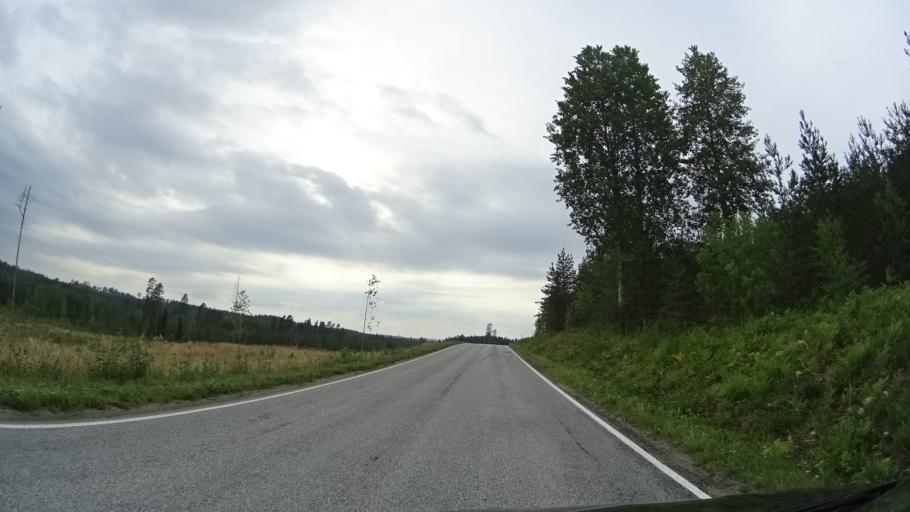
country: FI
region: Southern Savonia
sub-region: Savonlinna
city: Punkaharju
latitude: 61.7516
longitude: 29.4656
